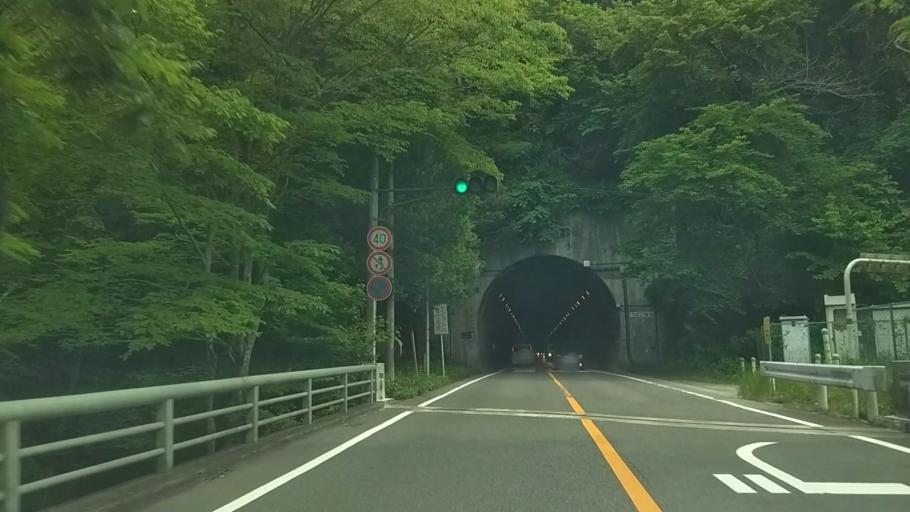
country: JP
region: Yamanashi
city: Isawa
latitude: 35.5572
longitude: 138.5908
